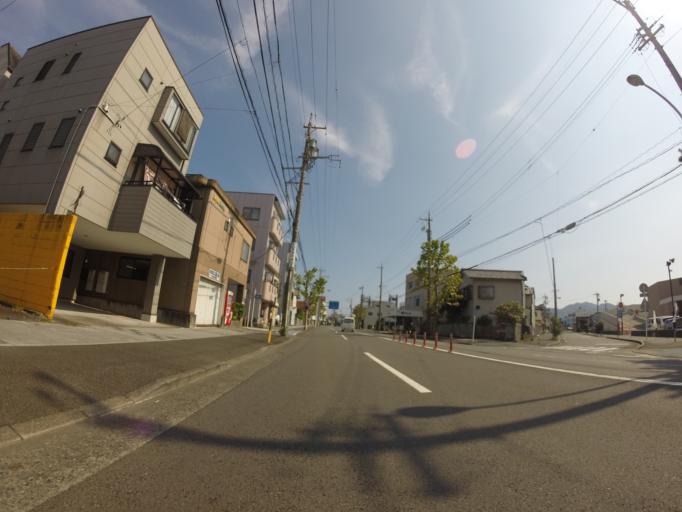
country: JP
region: Shizuoka
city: Shizuoka-shi
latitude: 34.9656
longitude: 138.3706
